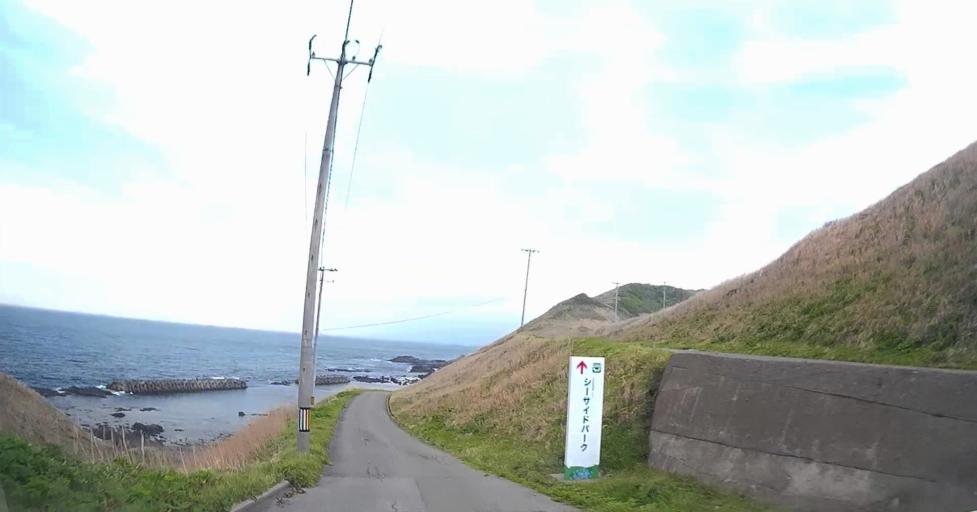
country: JP
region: Aomori
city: Shimokizukuri
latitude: 41.2503
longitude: 140.3444
